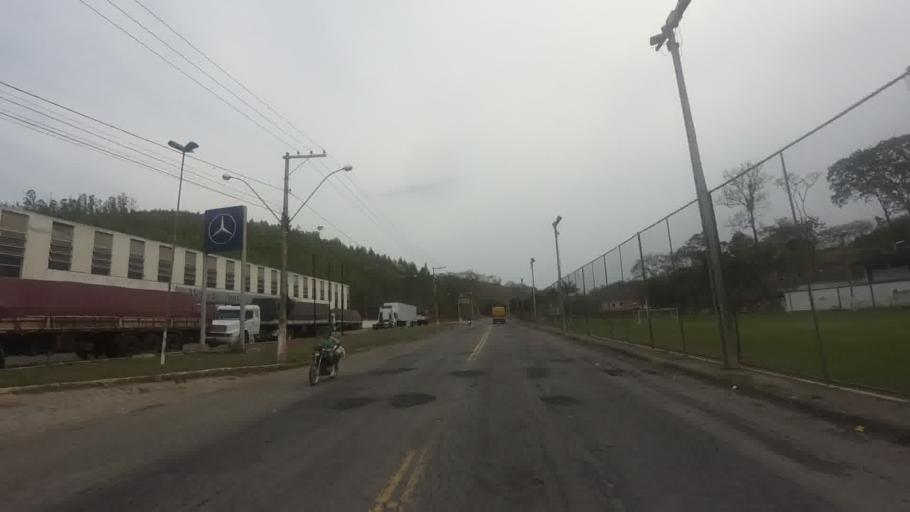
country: BR
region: Rio de Janeiro
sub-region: Santo Antonio De Padua
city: Santo Antonio de Padua
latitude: -21.5627
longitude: -42.1895
